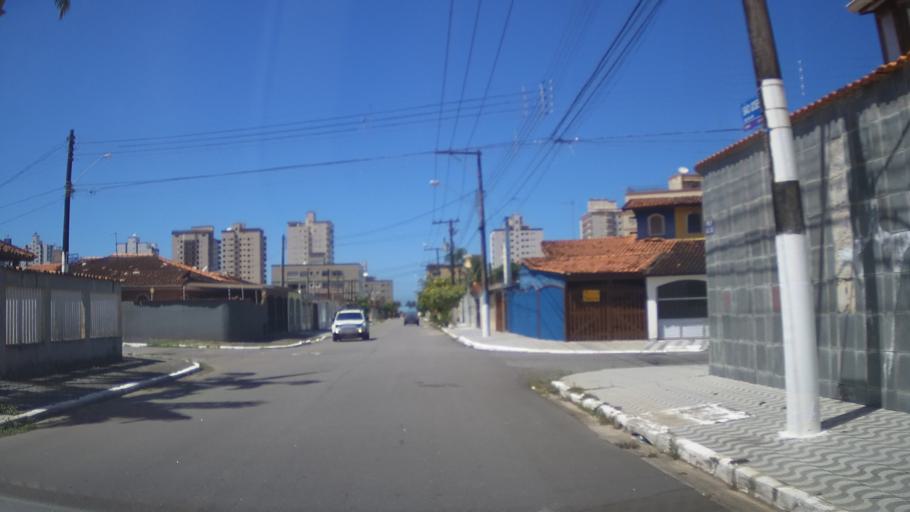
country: BR
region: Sao Paulo
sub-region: Mongagua
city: Mongagua
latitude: -24.0465
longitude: -46.5233
